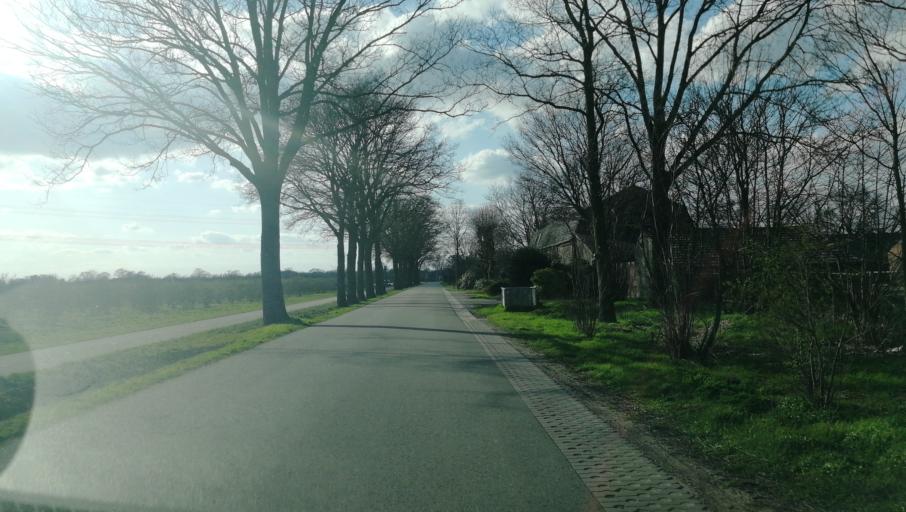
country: NL
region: Limburg
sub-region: Gemeente Venlo
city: Arcen
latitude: 51.4375
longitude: 6.0989
